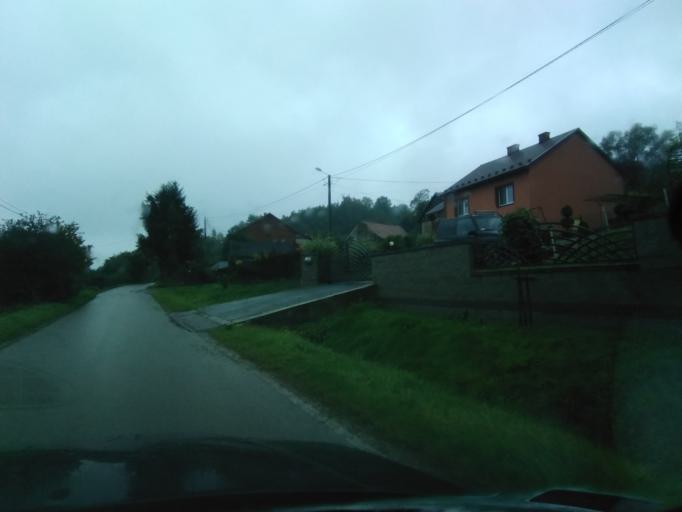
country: PL
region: Subcarpathian Voivodeship
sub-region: Powiat ropczycko-sedziszowski
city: Niedzwiada
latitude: 50.0125
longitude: 21.5476
